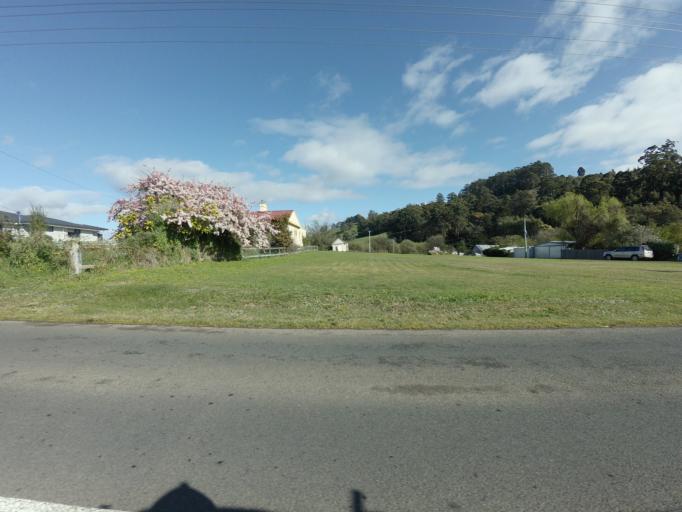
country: AU
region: Tasmania
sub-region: Huon Valley
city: Cygnet
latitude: -43.3166
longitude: 147.0112
